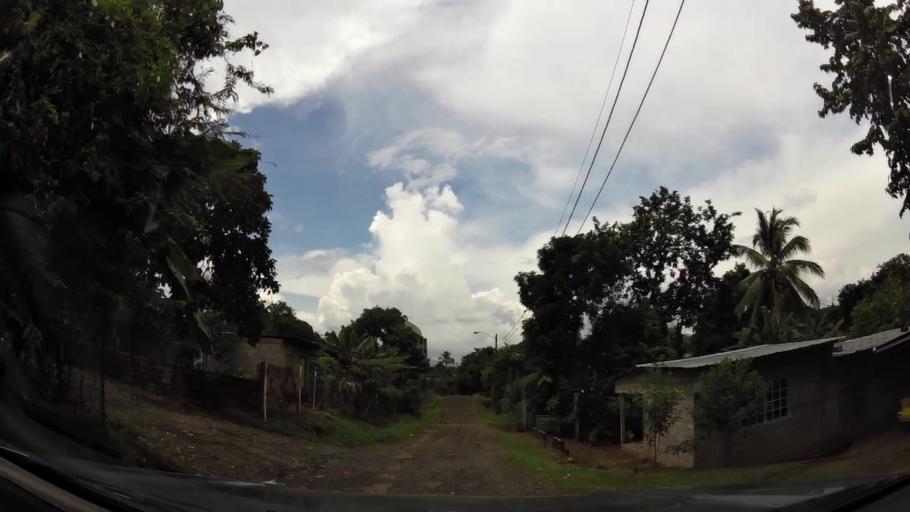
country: PA
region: Panama
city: Cabra Numero Uno
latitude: 9.1069
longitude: -79.3232
